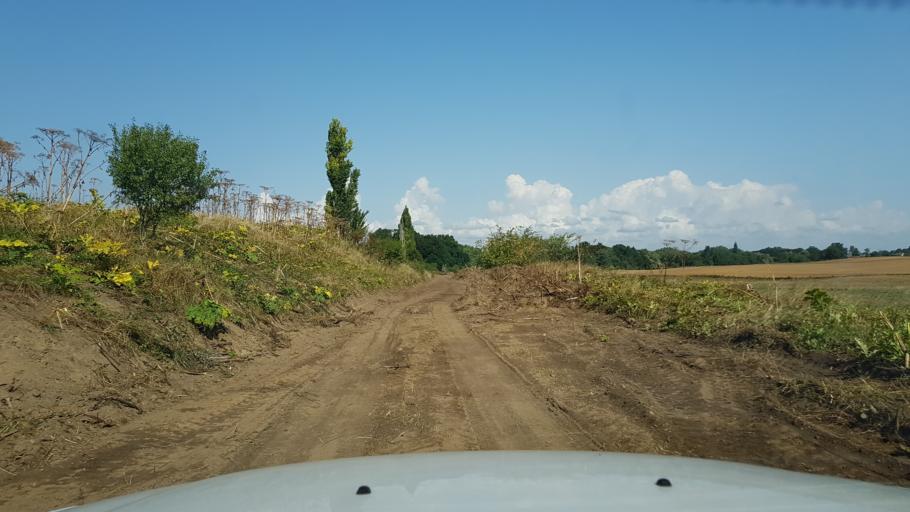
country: PL
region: West Pomeranian Voivodeship
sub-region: Powiat choszczenski
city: Pelczyce
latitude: 53.0804
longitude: 15.3033
